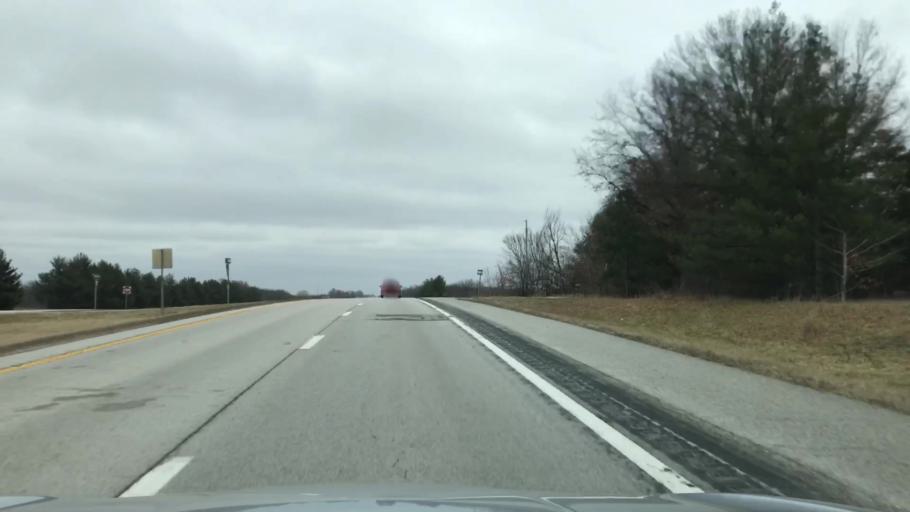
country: US
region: Missouri
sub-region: Livingston County
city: Chillicothe
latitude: 39.7771
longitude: -93.3691
